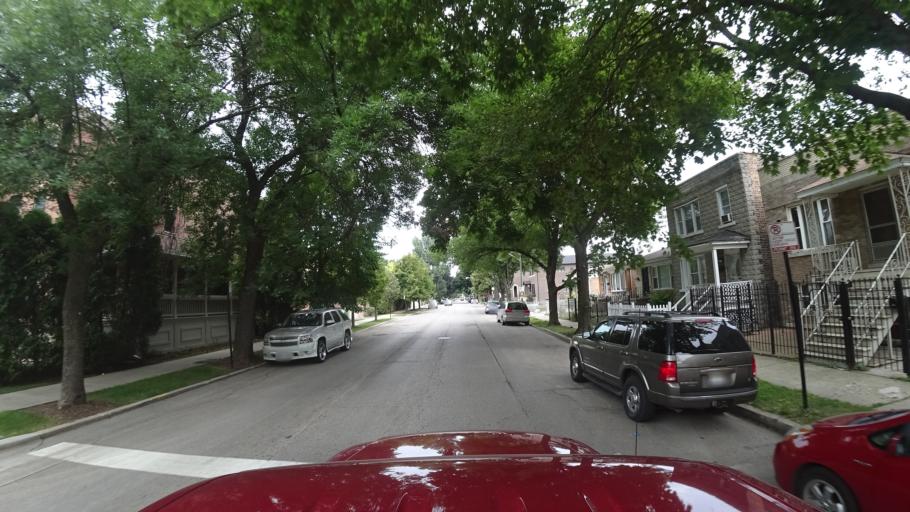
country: US
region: Illinois
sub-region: Cook County
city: Chicago
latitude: 41.8334
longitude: -87.6559
